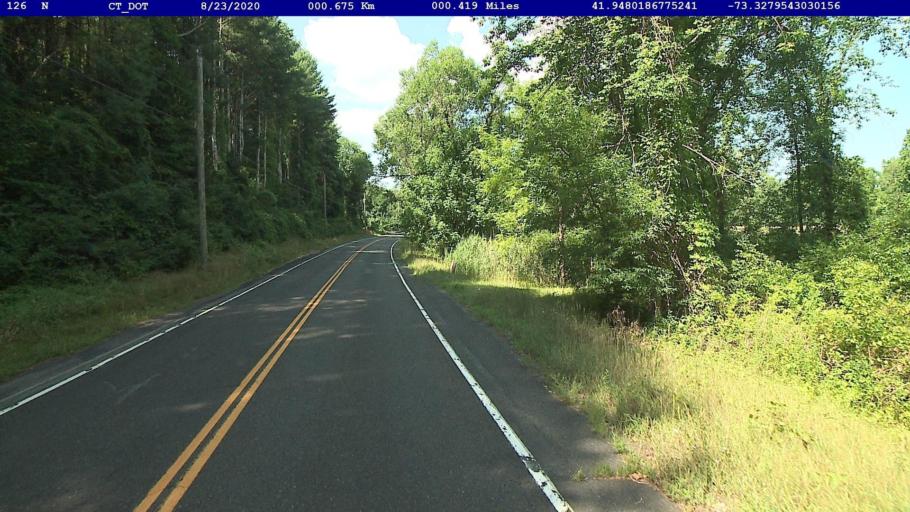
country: US
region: Connecticut
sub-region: Litchfield County
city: Canaan
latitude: 41.9482
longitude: -73.3280
